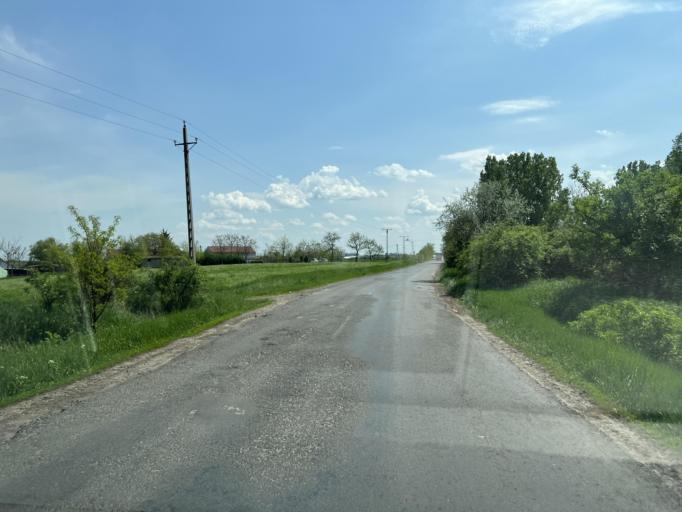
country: HU
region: Pest
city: Cegled
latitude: 47.2088
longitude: 19.7813
